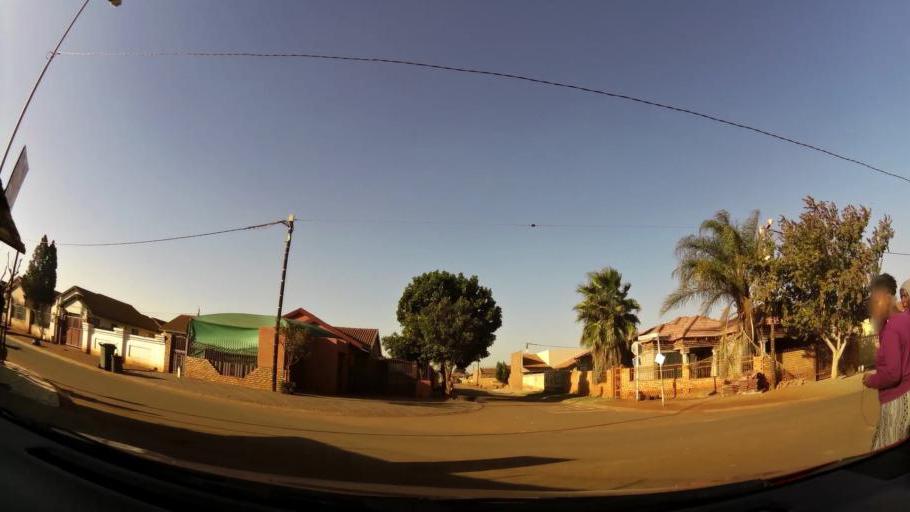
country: ZA
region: Gauteng
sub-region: City of Tshwane Metropolitan Municipality
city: Mabopane
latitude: -25.5881
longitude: 28.0949
